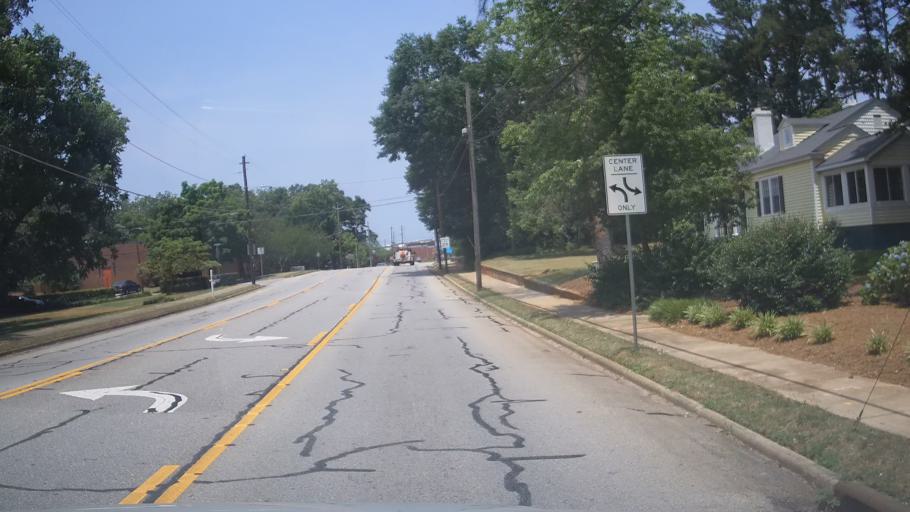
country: US
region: Georgia
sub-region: Hart County
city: Hartwell
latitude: 34.3491
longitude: -82.9296
